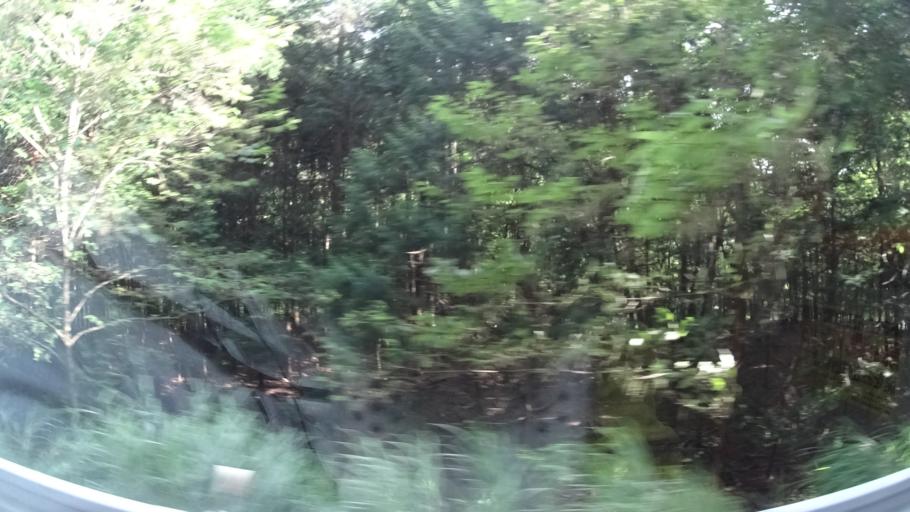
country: JP
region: Tochigi
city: Nikko
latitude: 36.6863
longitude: 139.4966
